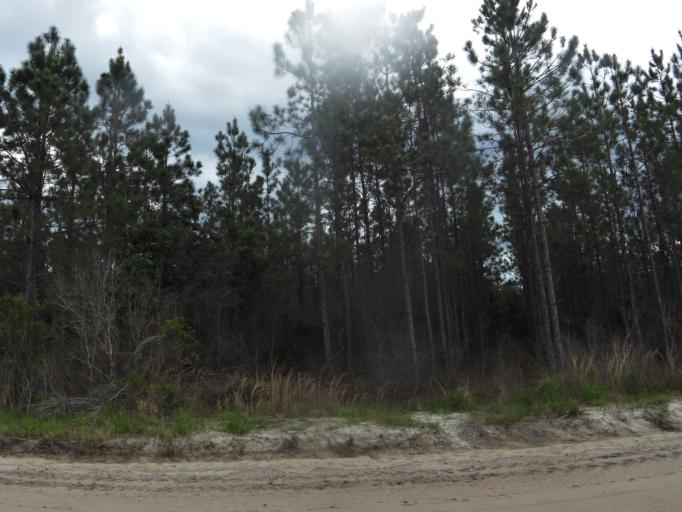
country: US
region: Georgia
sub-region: Charlton County
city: Folkston
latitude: 30.9424
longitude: -82.0036
